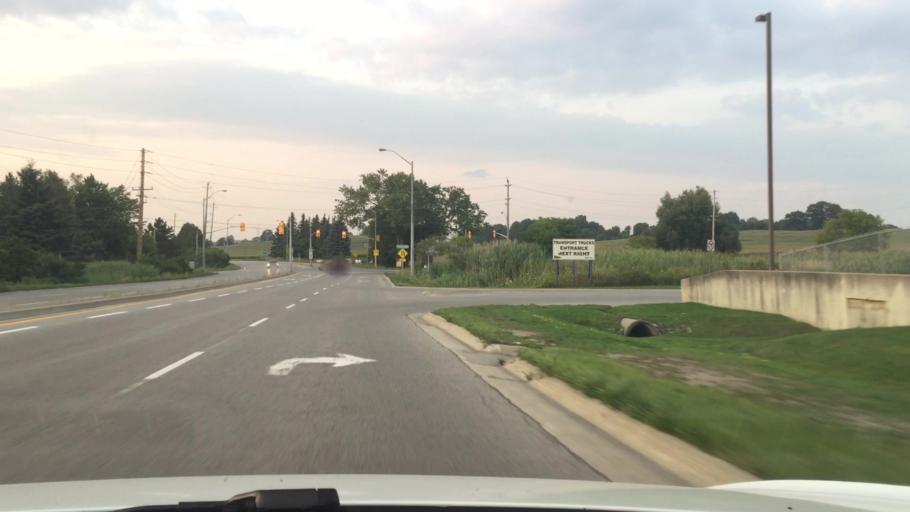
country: CA
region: Ontario
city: Cobourg
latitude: 43.9731
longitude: -78.2877
